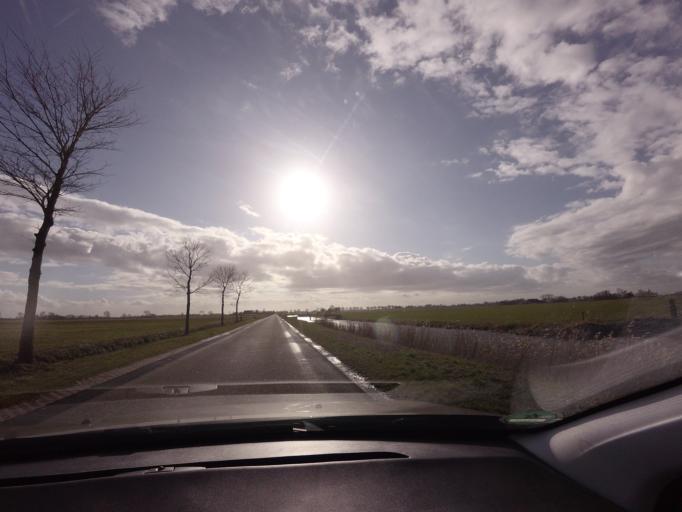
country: NL
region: Friesland
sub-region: Sudwest Fryslan
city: Oppenhuizen
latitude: 53.0460
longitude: 5.7195
